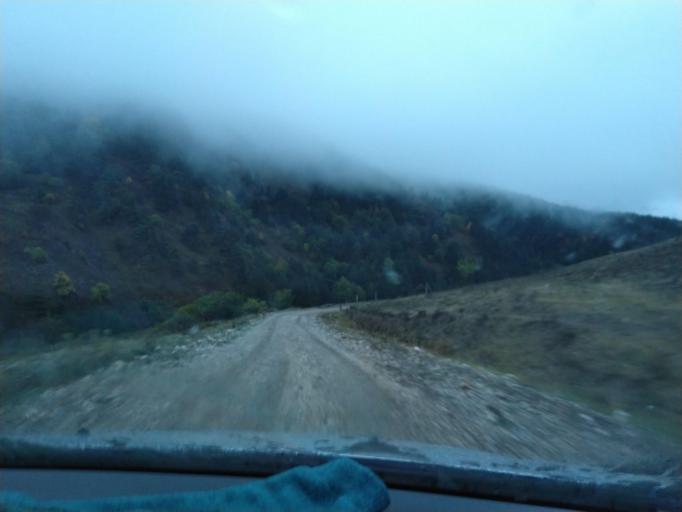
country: RU
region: North Ossetia
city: Tarskoye
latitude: 42.8266
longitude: 44.9758
